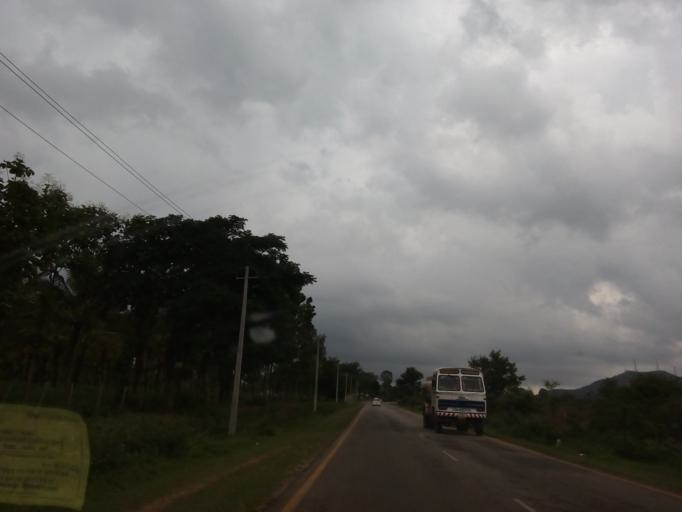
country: IN
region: Karnataka
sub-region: Hassan
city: Hassan
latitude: 13.0758
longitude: 76.0467
